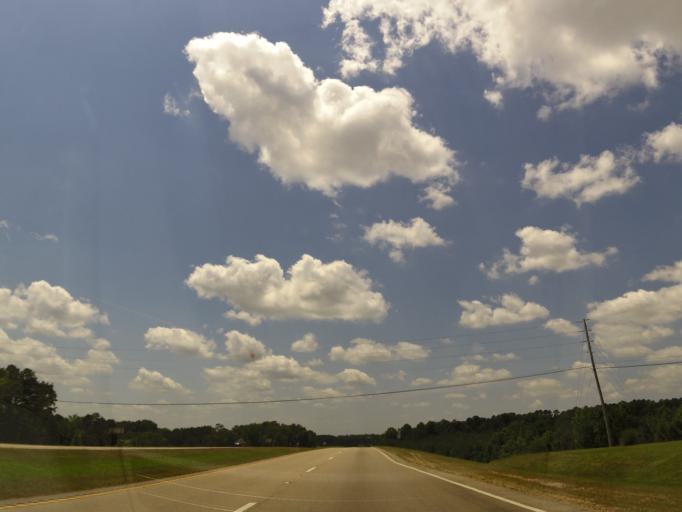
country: US
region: Mississippi
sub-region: Pontotoc County
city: Pontotoc
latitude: 34.2896
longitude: -88.9949
